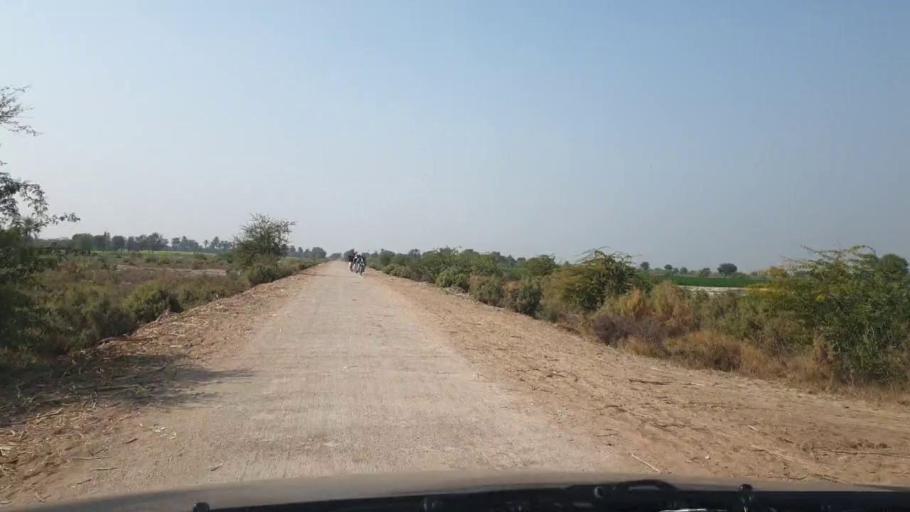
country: PK
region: Sindh
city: Jhol
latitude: 25.8922
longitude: 68.9385
